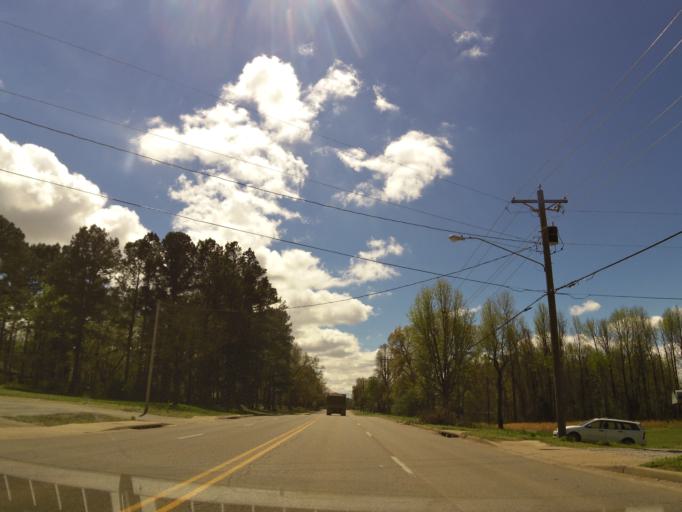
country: US
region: Arkansas
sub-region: Craighead County
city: Jonesboro
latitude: 35.8767
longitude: -90.7027
